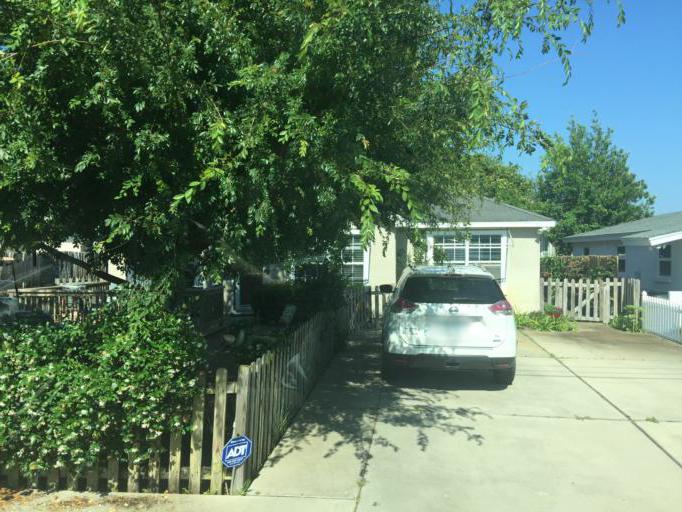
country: US
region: Florida
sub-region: Bay County
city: Panama City Beach
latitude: 30.2049
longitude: -85.8463
